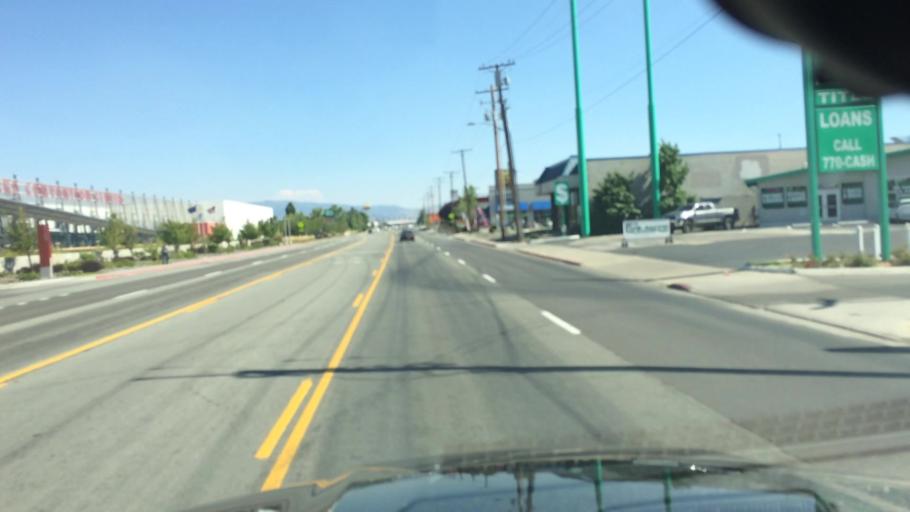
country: US
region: Nevada
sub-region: Washoe County
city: Reno
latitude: 39.4867
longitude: -119.7940
